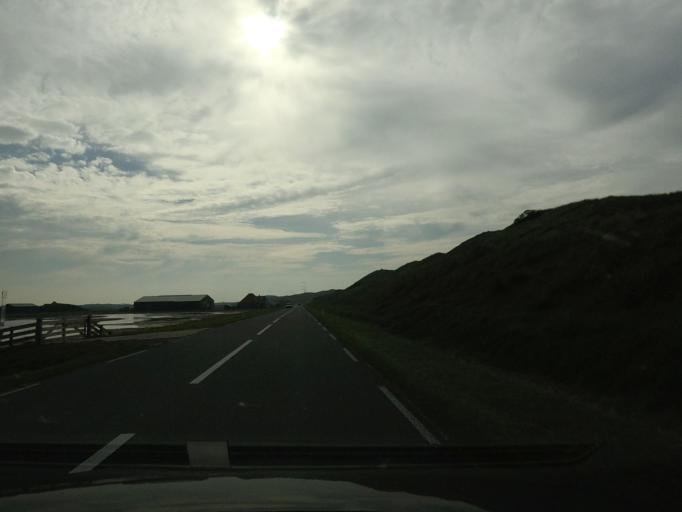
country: NL
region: North Holland
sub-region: Gemeente Den Helder
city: Den Helder
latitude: 52.8572
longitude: 4.7036
